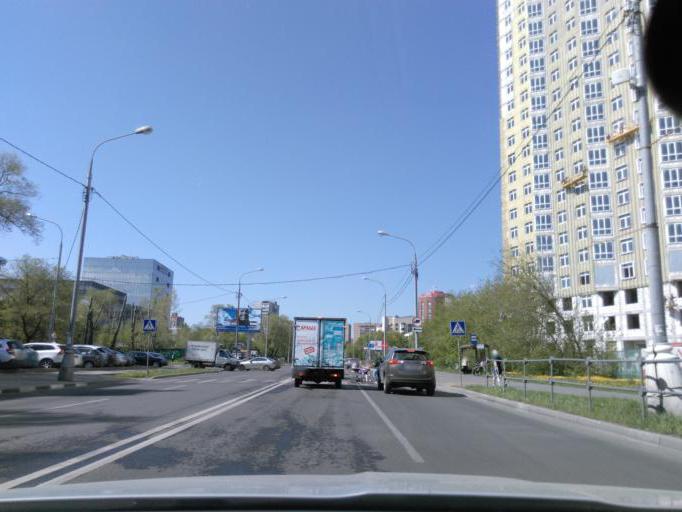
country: RU
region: Moscow
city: Golovinskiy
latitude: 55.8533
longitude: 37.4988
